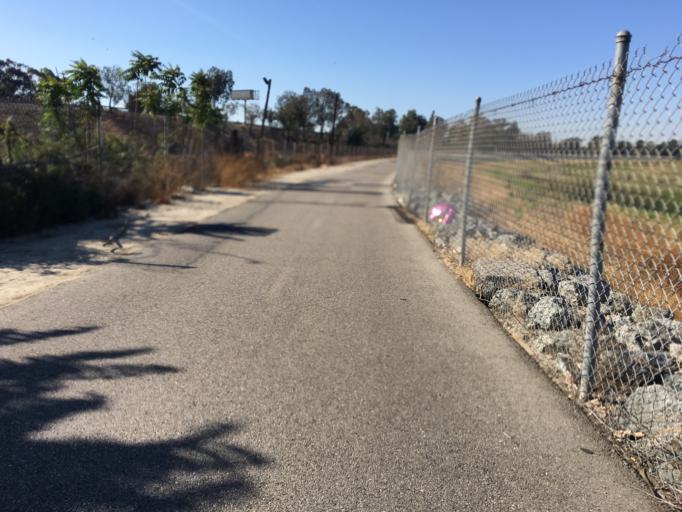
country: US
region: California
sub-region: Los Angeles County
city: Santa Fe Springs
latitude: 33.9622
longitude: -118.0870
